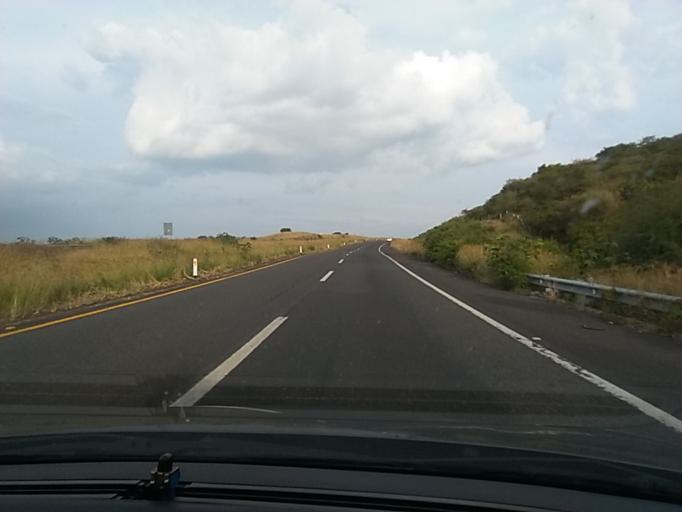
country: MX
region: Mexico
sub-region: Chapultepec
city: Chucandiro
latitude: 19.9036
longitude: -101.2744
